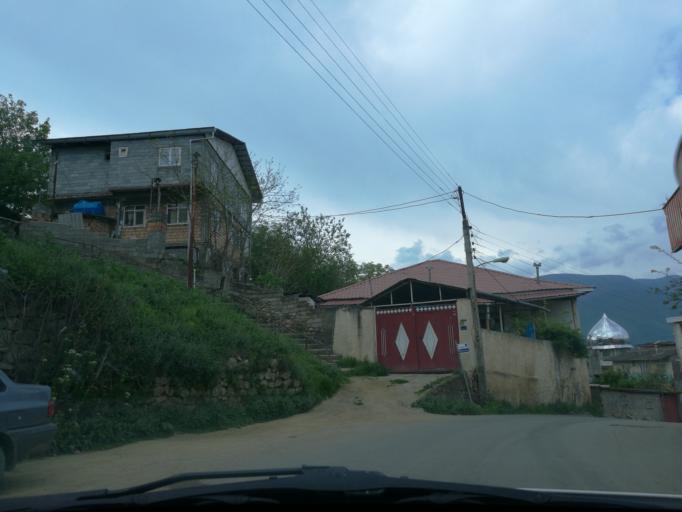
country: IR
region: Mazandaran
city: Chalus
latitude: 36.5310
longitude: 51.2297
